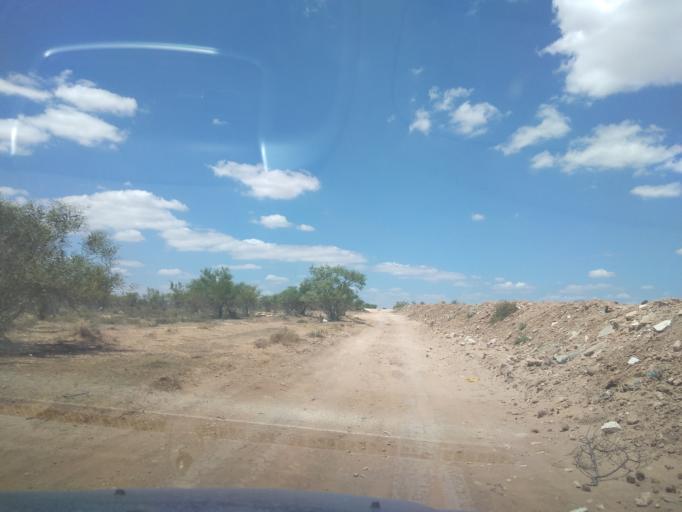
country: TN
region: Susah
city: Harqalah
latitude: 36.1649
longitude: 10.4478
